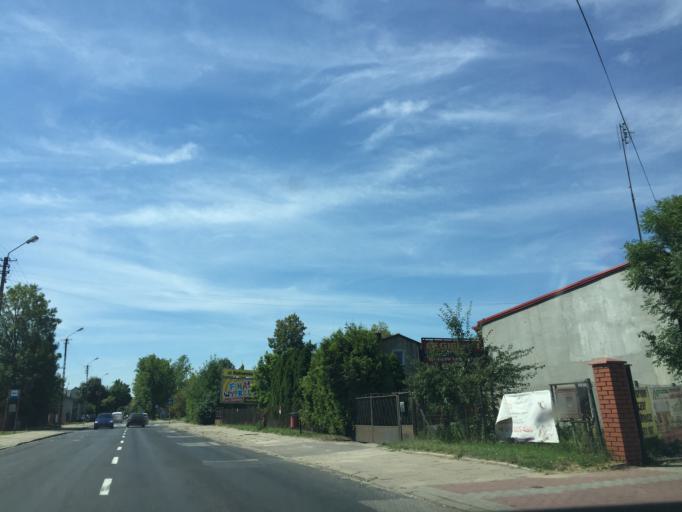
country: PL
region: Lodz Voivodeship
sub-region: Piotrkow Trybunalski
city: Piotrkow Trybunalski
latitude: 51.4125
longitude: 19.7082
